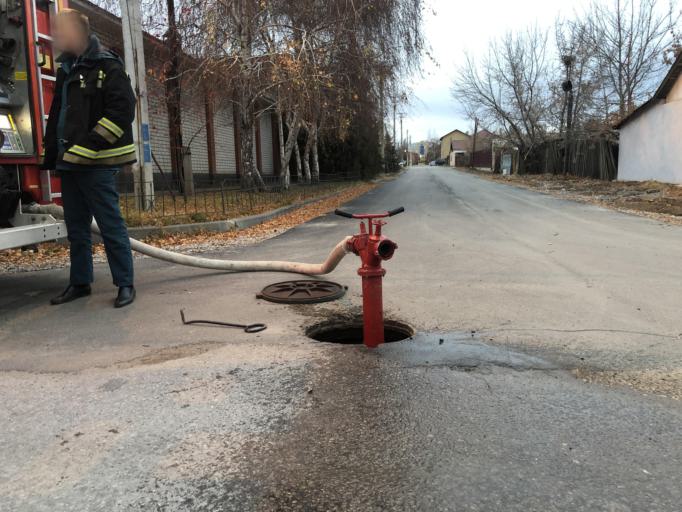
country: RU
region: Volgograd
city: Volgograd
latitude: 48.7366
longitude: 44.5139
